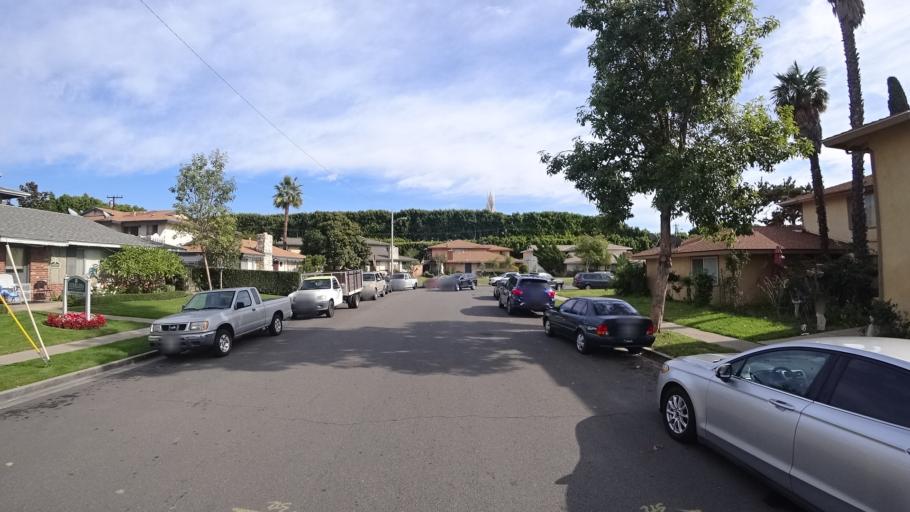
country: US
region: California
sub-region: Orange County
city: Garden Grove
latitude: 33.7881
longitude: -117.9029
